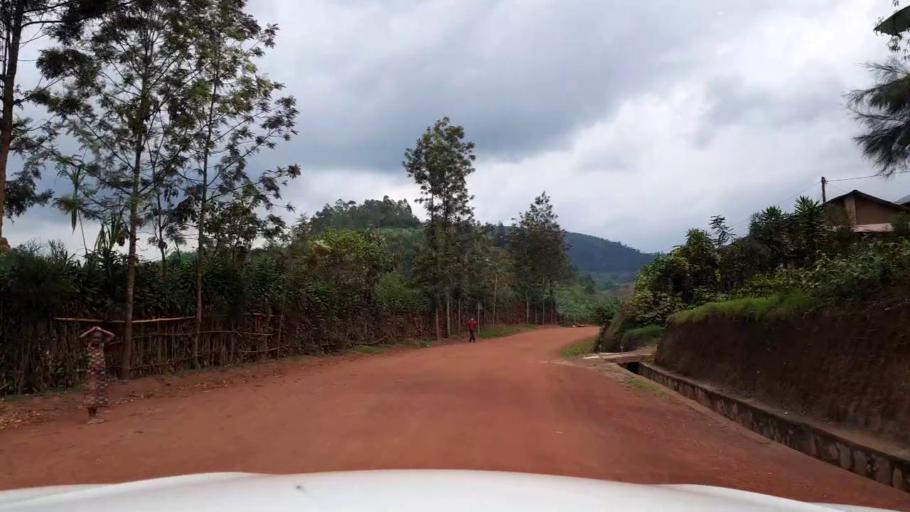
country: RW
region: Northern Province
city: Musanze
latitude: -1.6582
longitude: 29.7992
